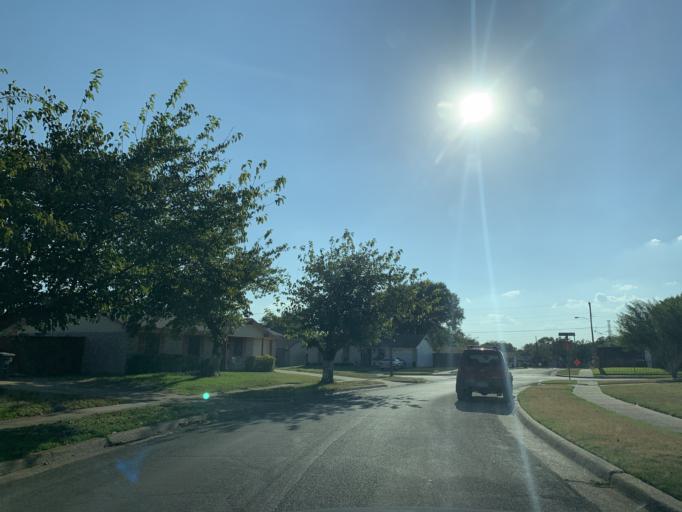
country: US
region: Texas
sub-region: Dallas County
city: Hutchins
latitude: 32.6634
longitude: -96.7653
